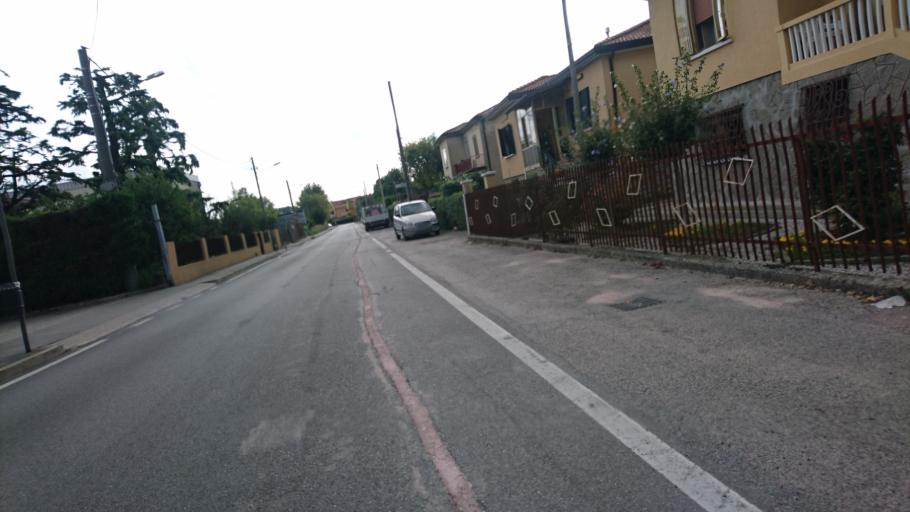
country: IT
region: Veneto
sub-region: Provincia di Padova
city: Sarmeola
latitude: 45.4310
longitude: 11.8425
